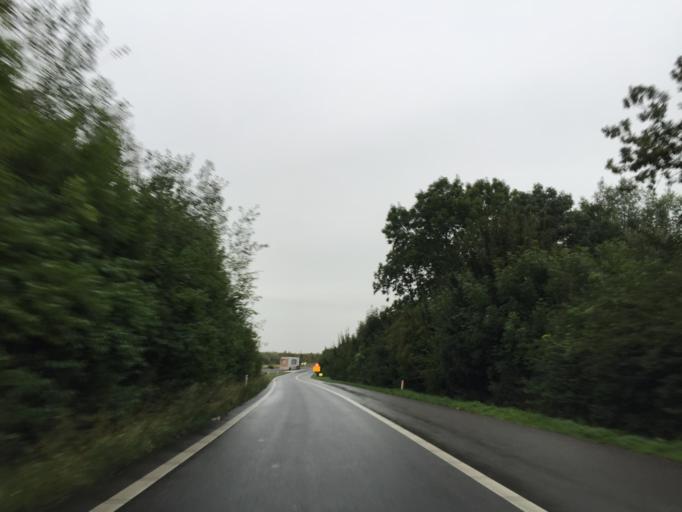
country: NL
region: Limburg
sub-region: Gemeente Maastricht
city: Heer
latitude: 50.8158
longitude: 5.7222
